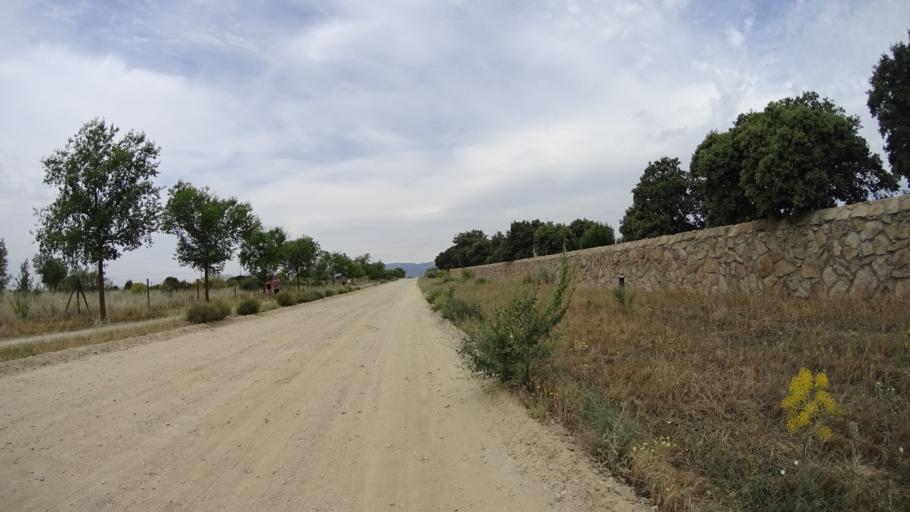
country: ES
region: Madrid
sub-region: Provincia de Madrid
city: Colmenarejo
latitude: 40.5693
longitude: -4.0284
